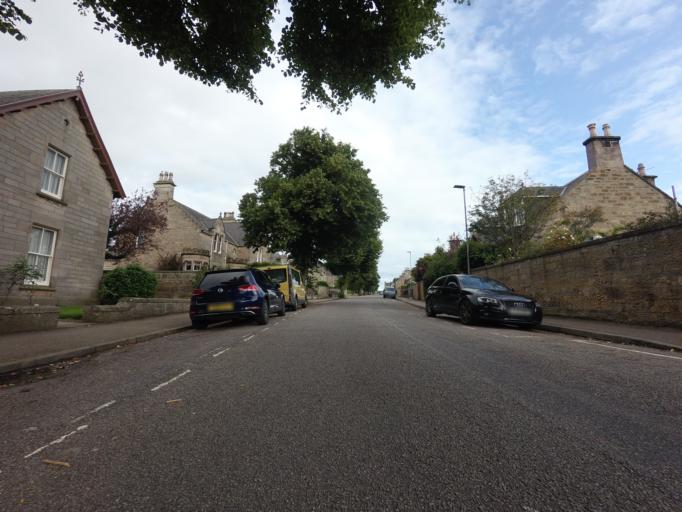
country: GB
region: Scotland
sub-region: Moray
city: Elgin
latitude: 57.6442
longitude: -3.3118
